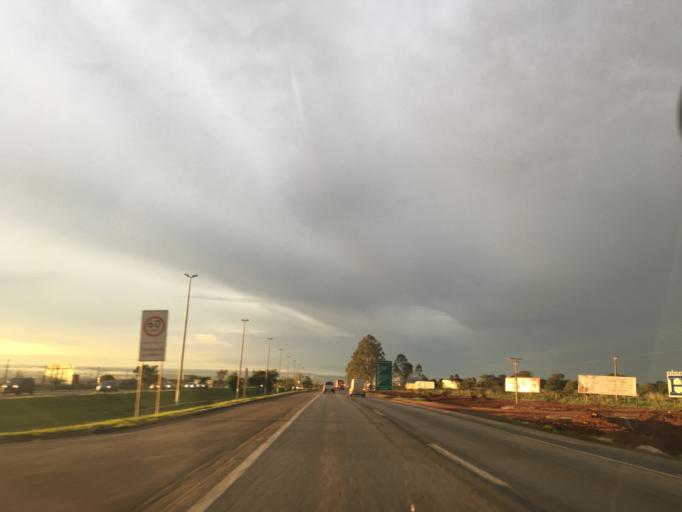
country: BR
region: Goias
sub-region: Luziania
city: Luziania
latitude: -16.0368
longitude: -47.9794
